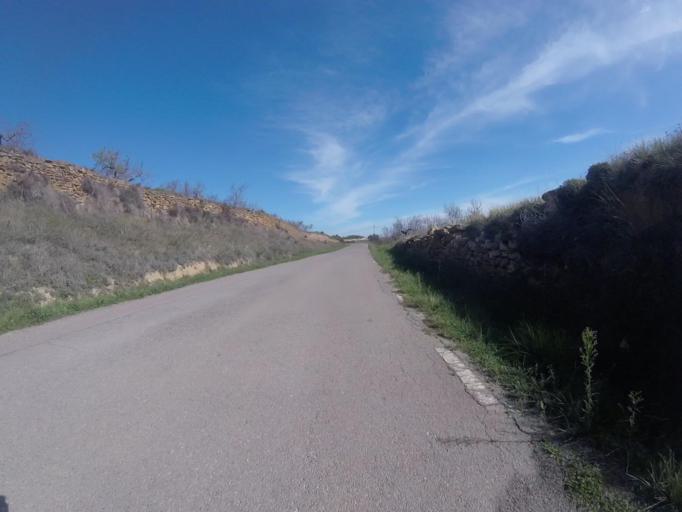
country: ES
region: Valencia
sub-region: Provincia de Castello
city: Sarratella
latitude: 40.3031
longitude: 0.0306
